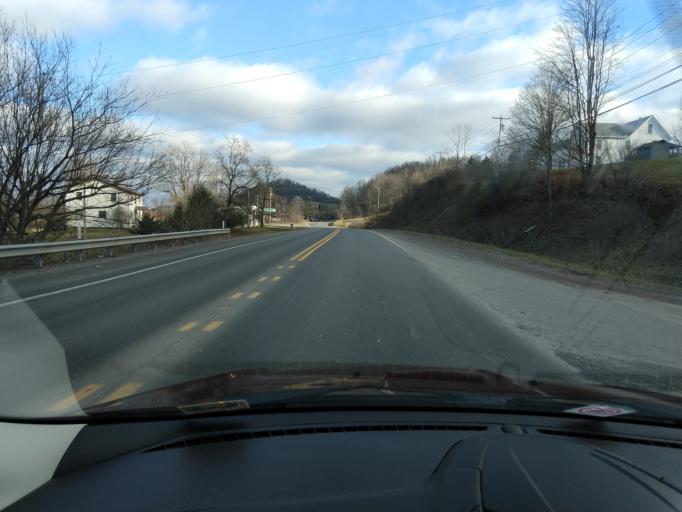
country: US
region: West Virginia
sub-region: Randolph County
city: Elkins
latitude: 38.8095
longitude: -79.8819
